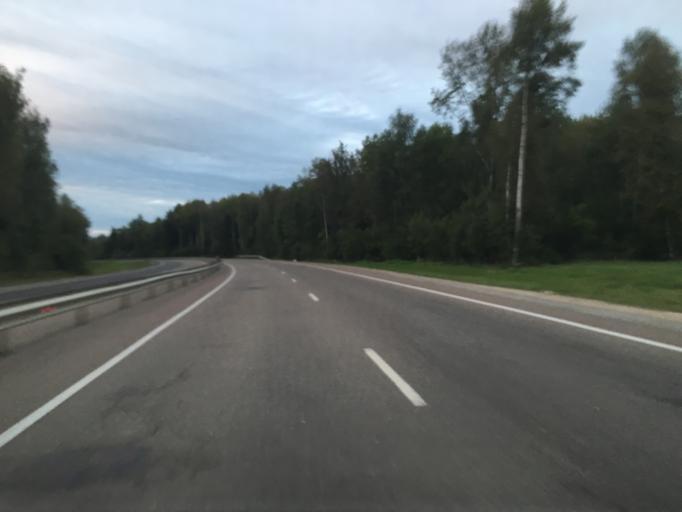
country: RU
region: Kaluga
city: Kaluga
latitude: 54.6393
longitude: 36.3001
